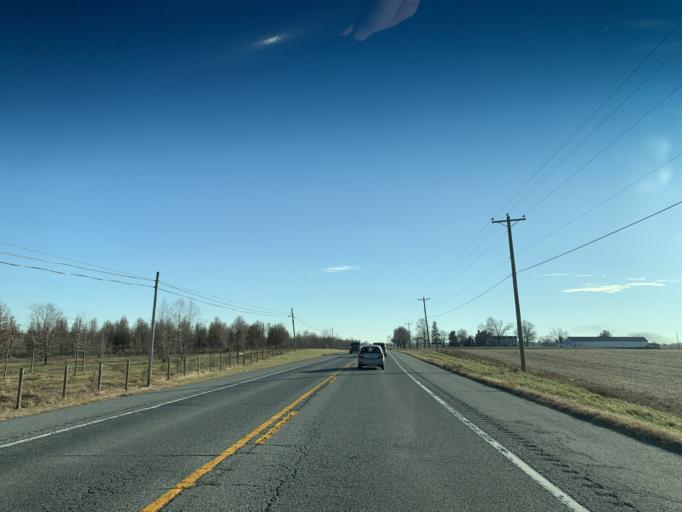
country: US
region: Delaware
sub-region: New Castle County
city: Middletown
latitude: 39.4267
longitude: -75.8605
